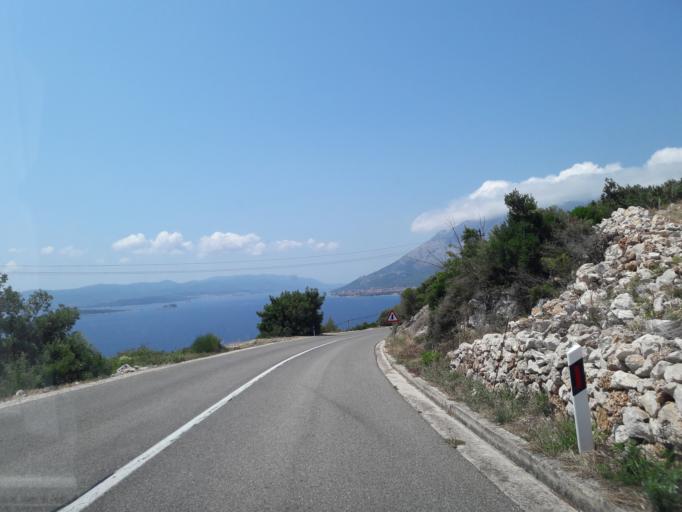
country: HR
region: Dubrovacko-Neretvanska
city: Orebic
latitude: 42.9735
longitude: 17.2392
